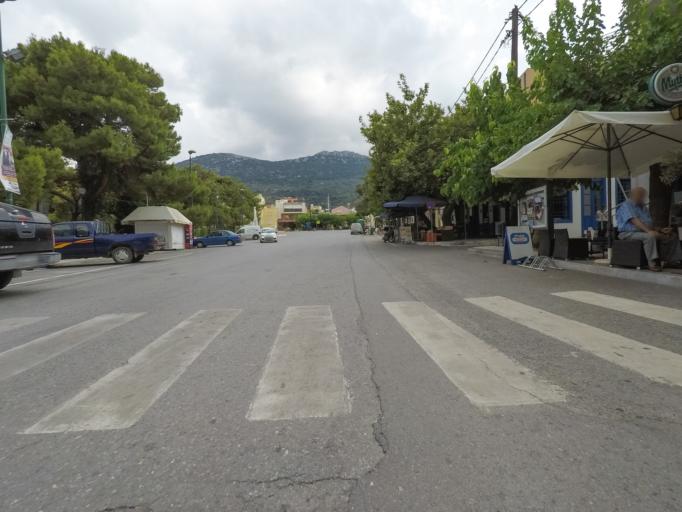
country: GR
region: Crete
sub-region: Nomos Lasithiou
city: Neapoli
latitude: 35.2564
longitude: 25.6071
